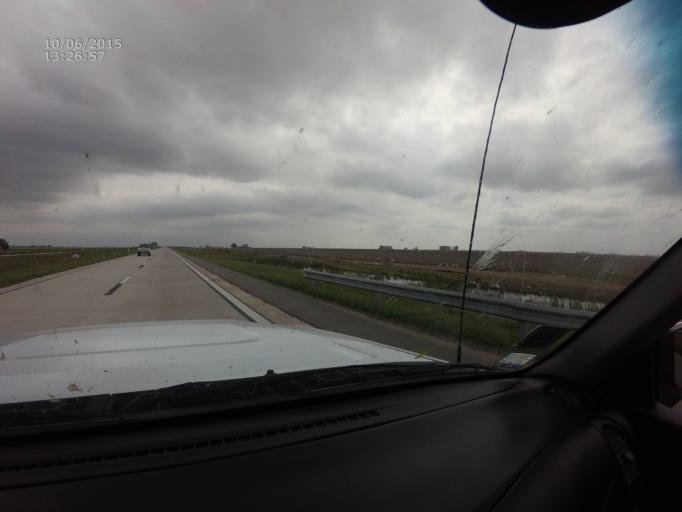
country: AR
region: Cordoba
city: Marcos Juarez
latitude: -32.6476
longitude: -62.1923
